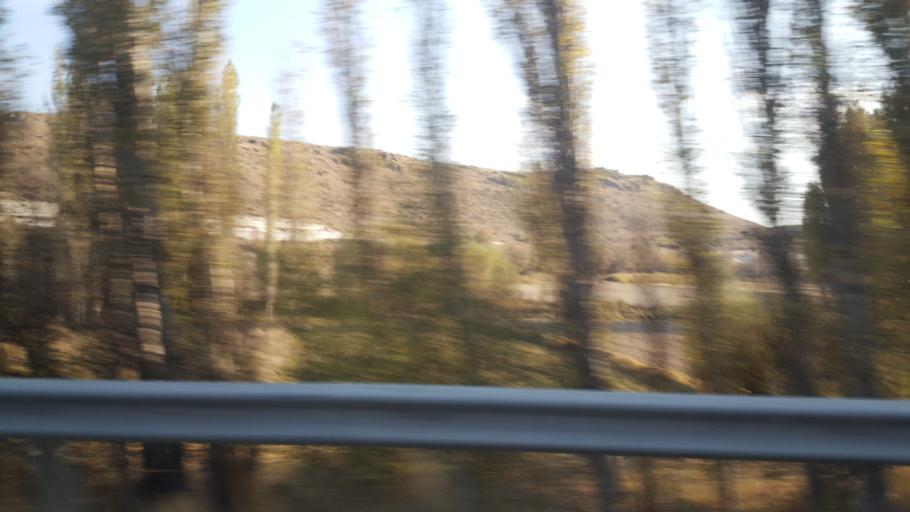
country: TR
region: Eskisehir
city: Seyitgazi
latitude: 39.4160
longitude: 30.6463
